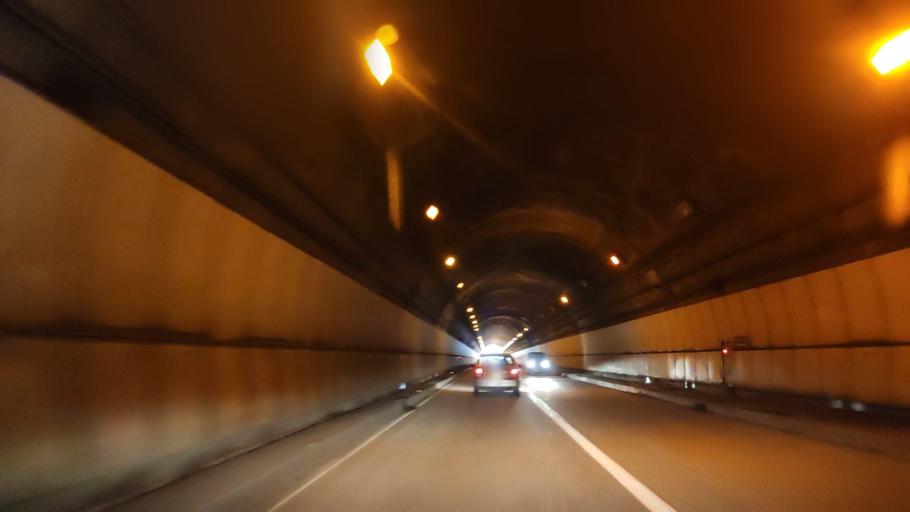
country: JP
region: Akita
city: Takanosu
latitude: 40.2187
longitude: 140.2558
